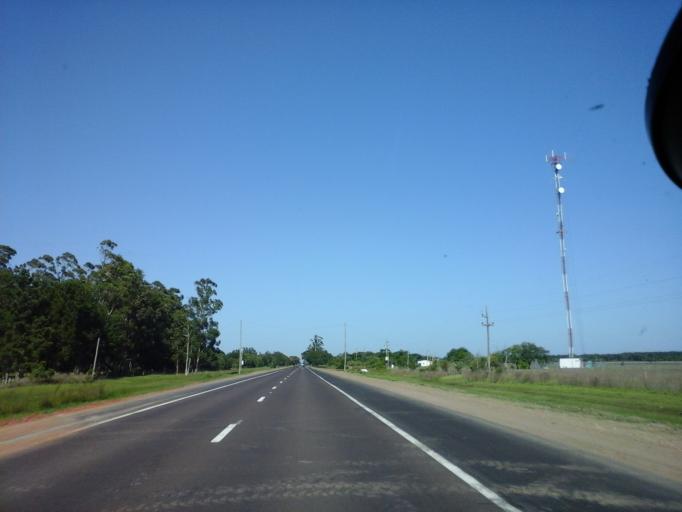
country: AR
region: Corrientes
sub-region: Departamento de Itati
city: Itati
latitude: -27.3667
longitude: -58.3354
